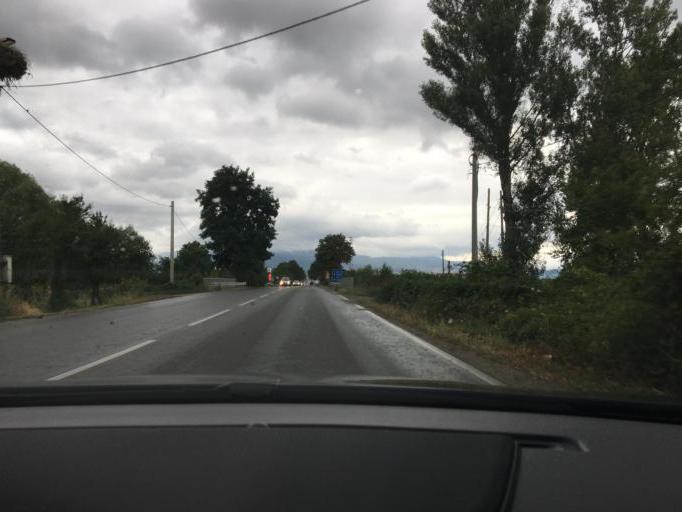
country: BG
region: Kyustendil
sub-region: Obshtina Kyustendil
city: Kyustendil
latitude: 42.2809
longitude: 22.7255
